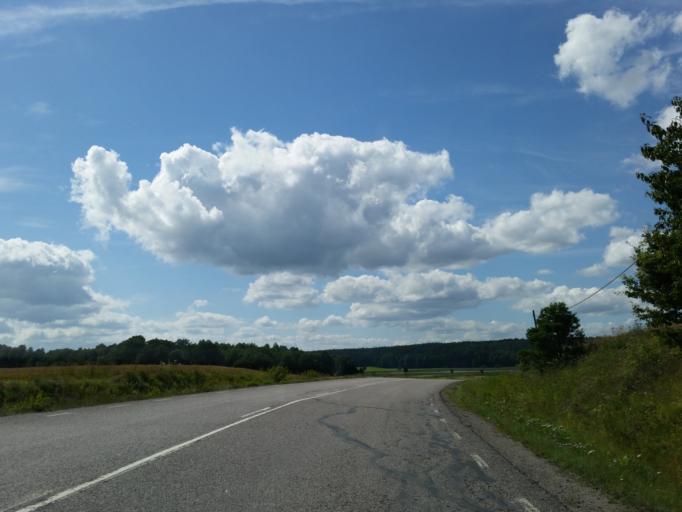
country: SE
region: Soedermanland
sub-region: Trosa Kommun
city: Vagnharad
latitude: 58.9869
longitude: 17.6344
